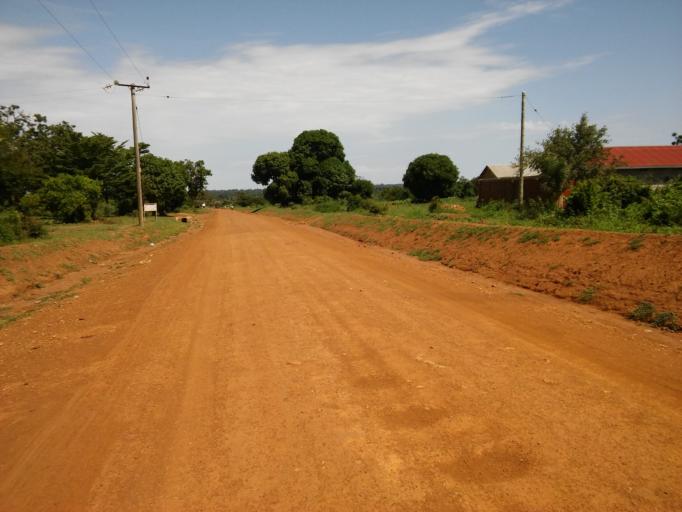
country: UG
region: Eastern Region
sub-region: Kumi District
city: Kumi
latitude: 1.4858
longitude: 33.9216
